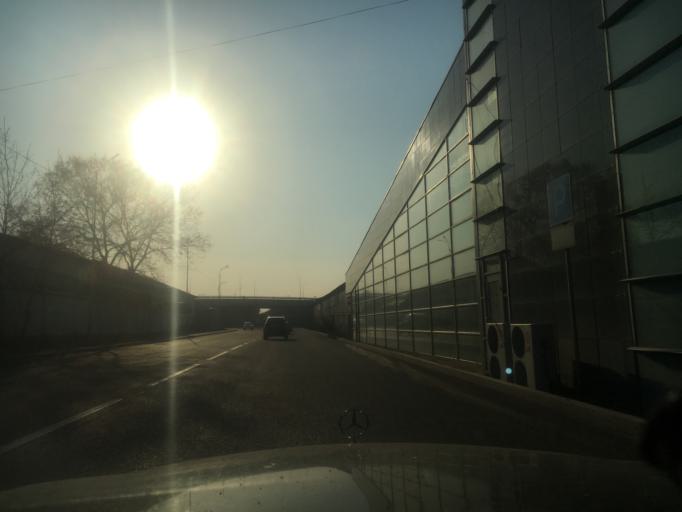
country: KZ
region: Almaty Qalasy
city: Almaty
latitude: 43.2761
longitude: 76.9479
